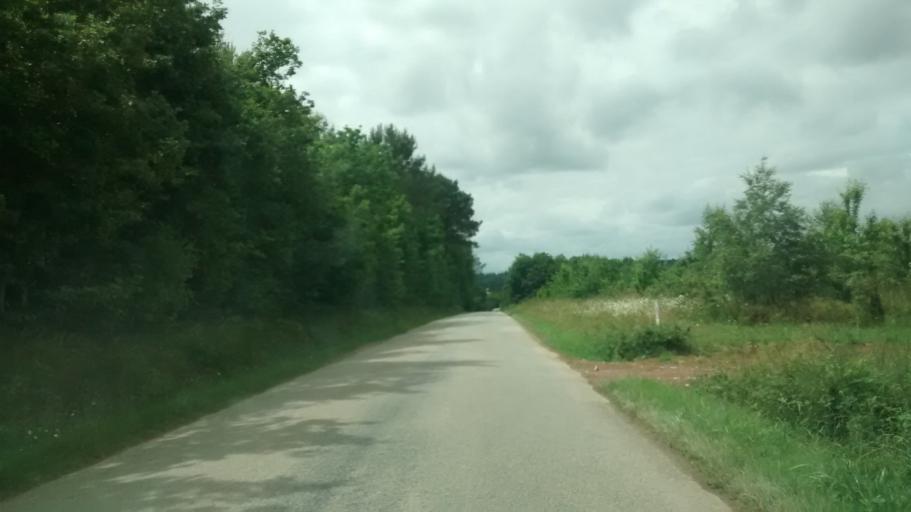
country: FR
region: Brittany
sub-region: Departement du Morbihan
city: Carentoir
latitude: 47.8223
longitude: -2.1564
